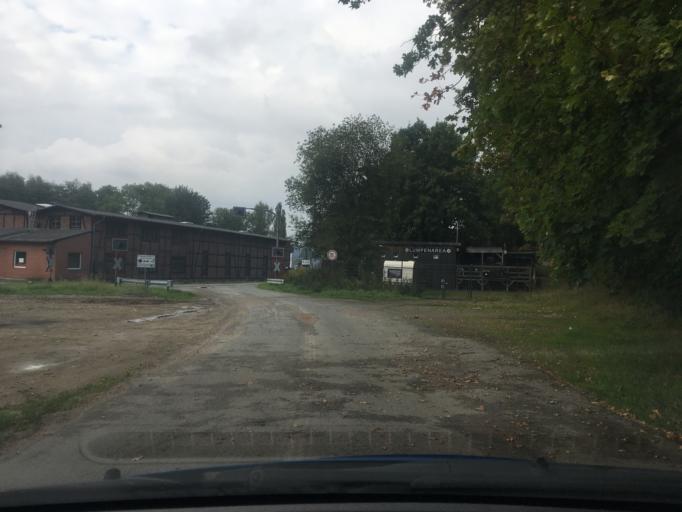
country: DE
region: Lower Saxony
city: Lueneburg
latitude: 53.2360
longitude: 10.4200
